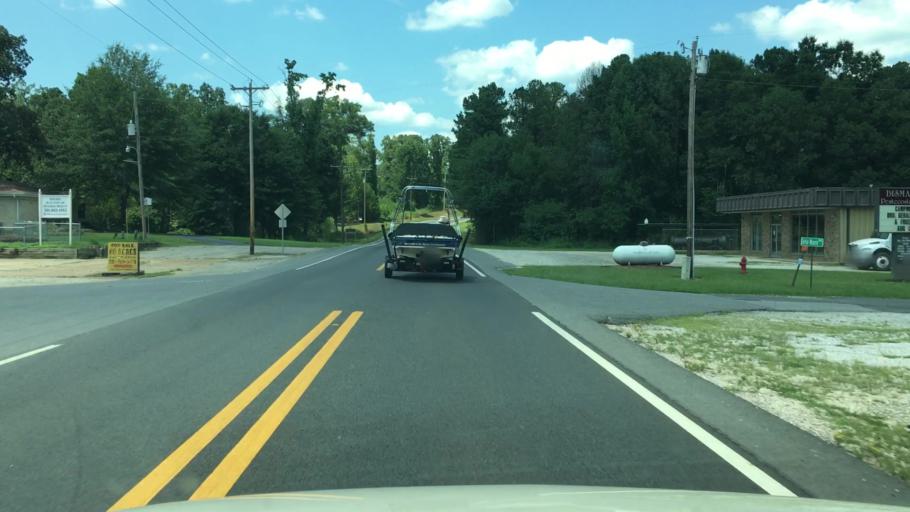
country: US
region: Arkansas
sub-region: Garland County
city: Lake Hamilton
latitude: 34.2840
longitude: -93.1632
